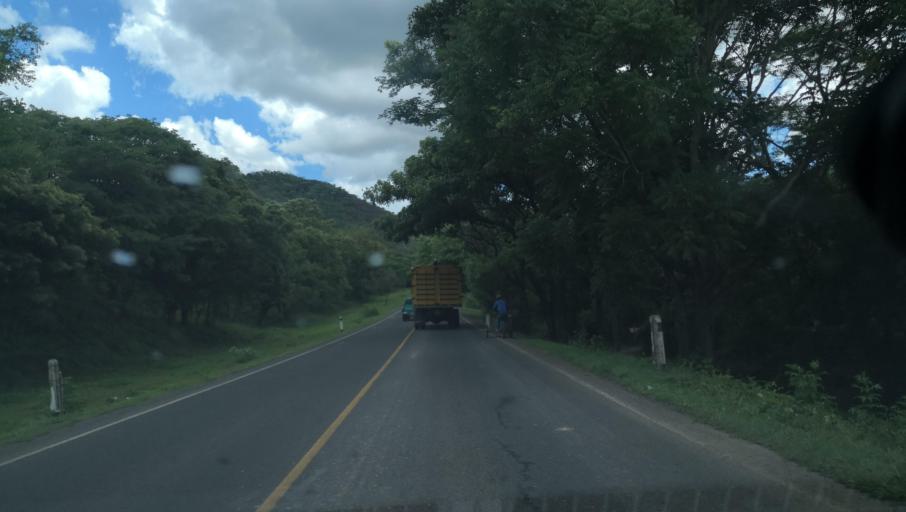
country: NI
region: Madriz
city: Yalaguina
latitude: 13.4589
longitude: -86.4630
